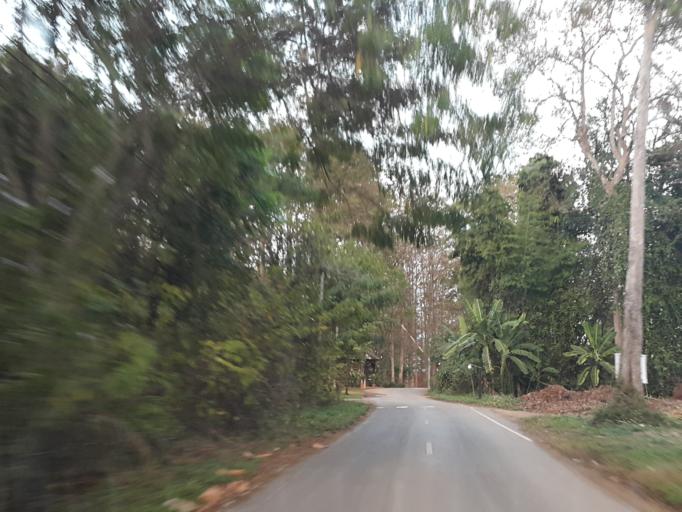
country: TH
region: Lampang
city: Mueang Pan
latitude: 18.8324
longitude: 99.4661
